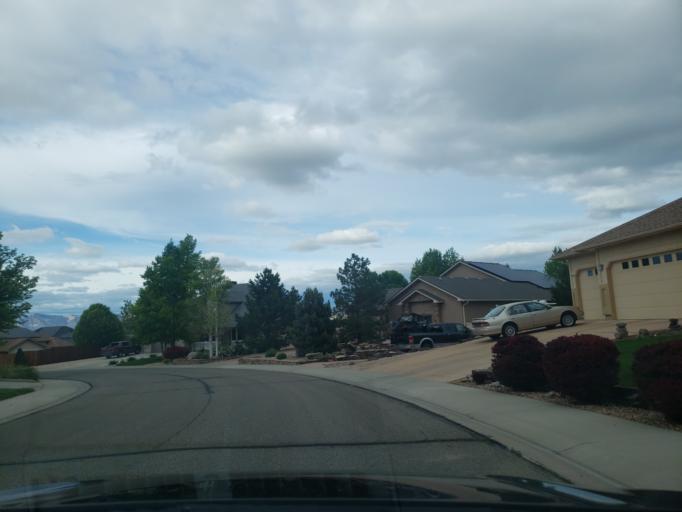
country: US
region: Colorado
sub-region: Mesa County
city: Redlands
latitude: 39.1044
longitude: -108.6649
